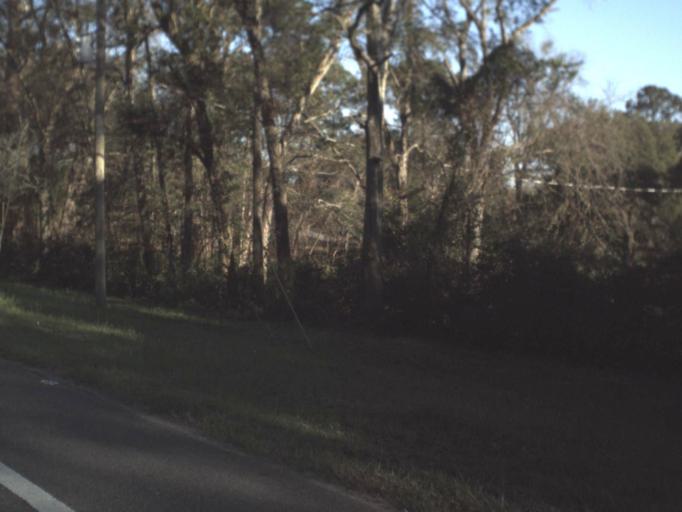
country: US
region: Florida
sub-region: Leon County
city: Tallahassee
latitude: 30.4912
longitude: -84.1270
